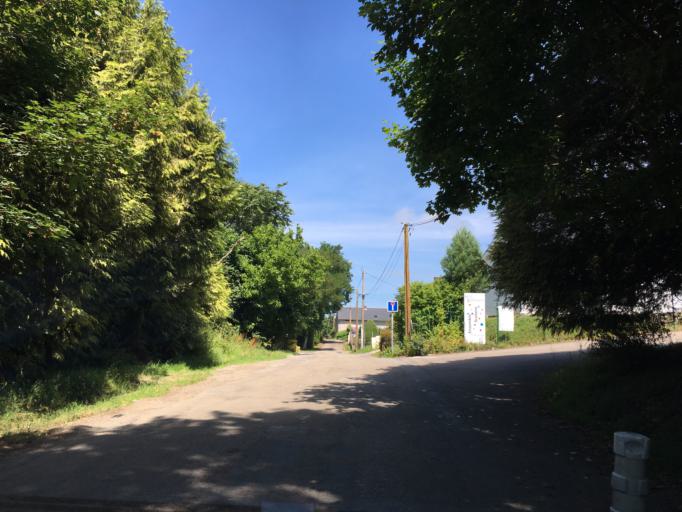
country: FR
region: Brittany
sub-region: Departement du Finistere
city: Quimper
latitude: 48.0098
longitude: -4.1112
